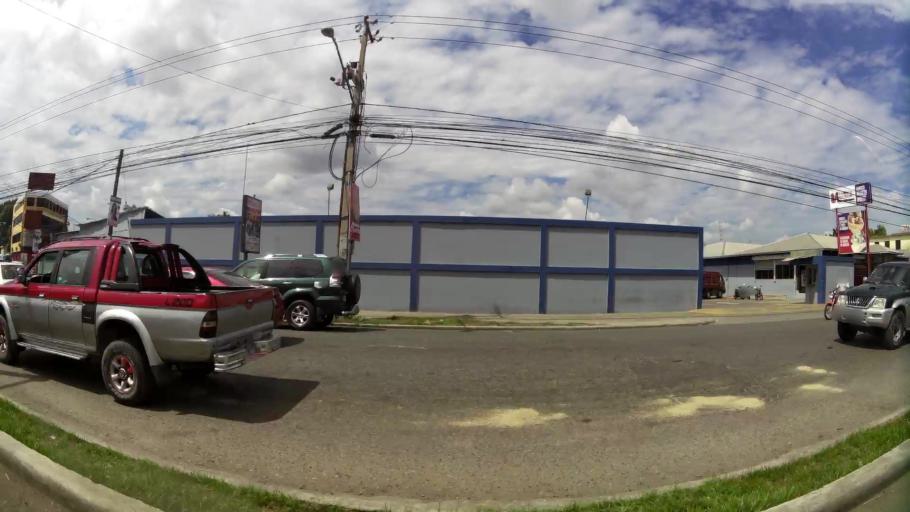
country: DO
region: Santiago
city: Santiago de los Caballeros
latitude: 19.4649
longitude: -70.7113
